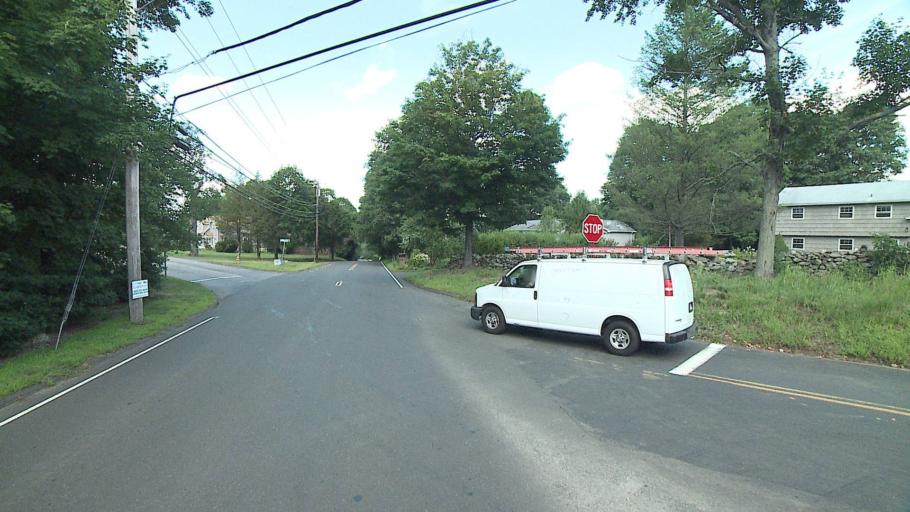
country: US
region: Connecticut
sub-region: Fairfield County
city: Trumbull
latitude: 41.2792
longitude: -73.1588
